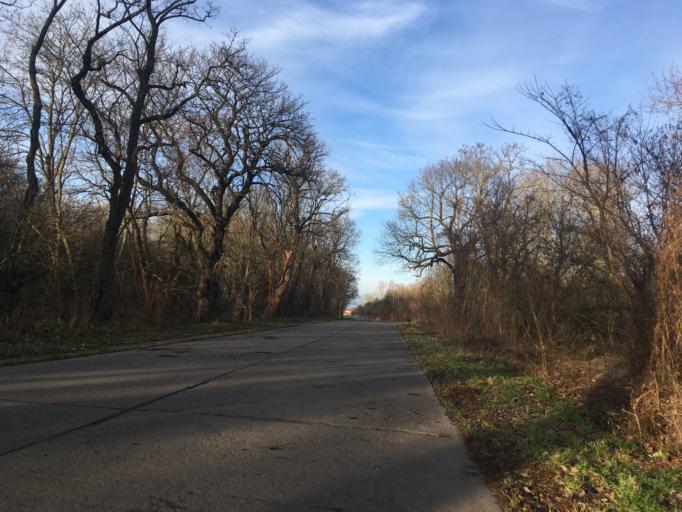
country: DE
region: Berlin
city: Blankenfelde
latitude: 52.6312
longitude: 13.4009
